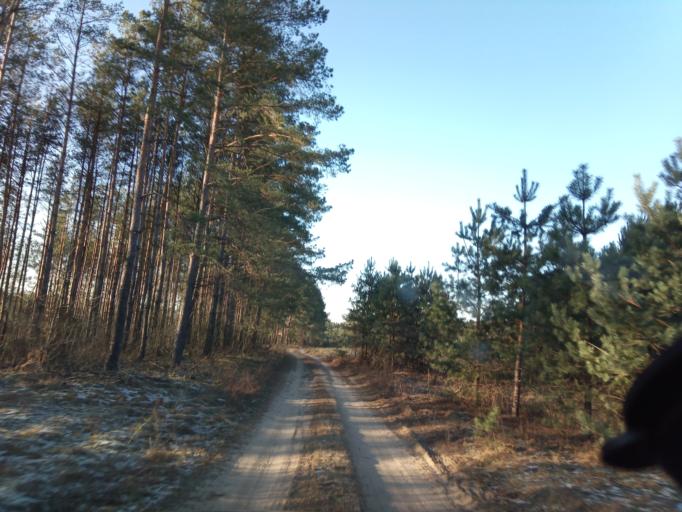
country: LT
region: Alytaus apskritis
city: Druskininkai
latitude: 53.9707
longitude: 23.9645
